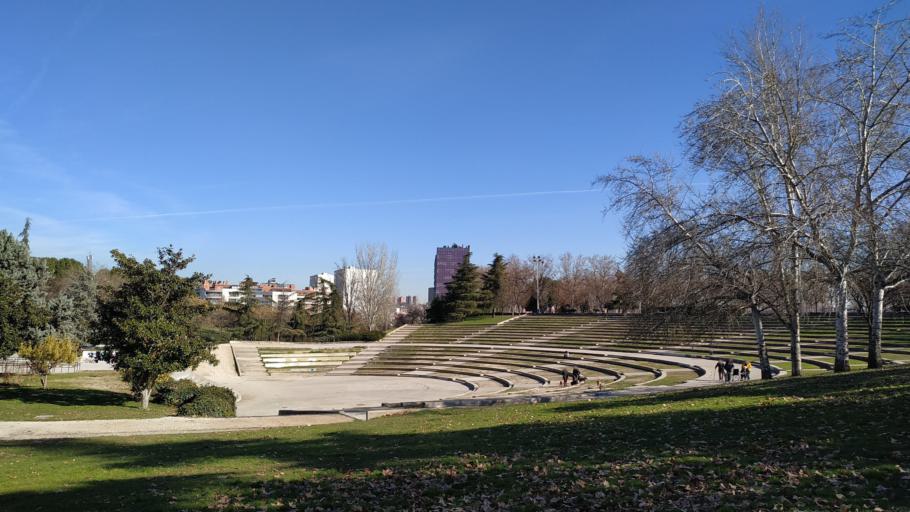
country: ES
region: Madrid
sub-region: Provincia de Madrid
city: Arganzuela
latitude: 40.3902
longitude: -3.6846
